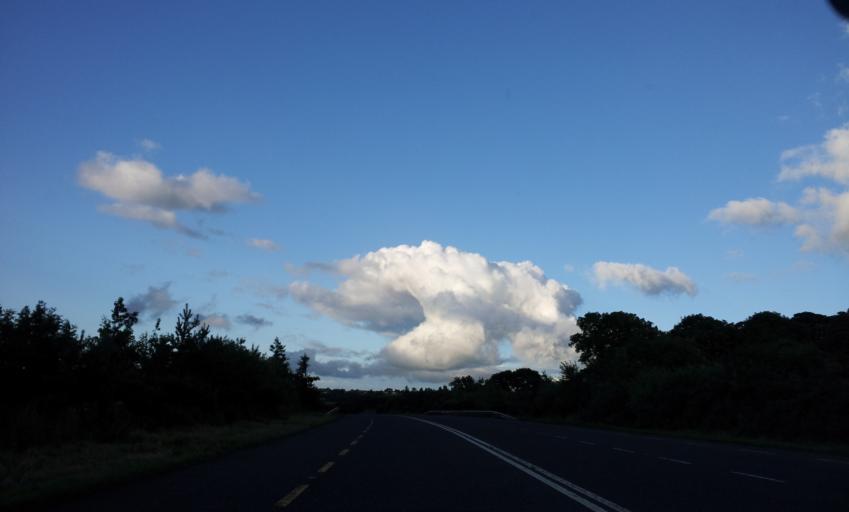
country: IE
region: Munster
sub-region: County Limerick
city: Abbeyfeale
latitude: 52.3471
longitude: -9.3363
